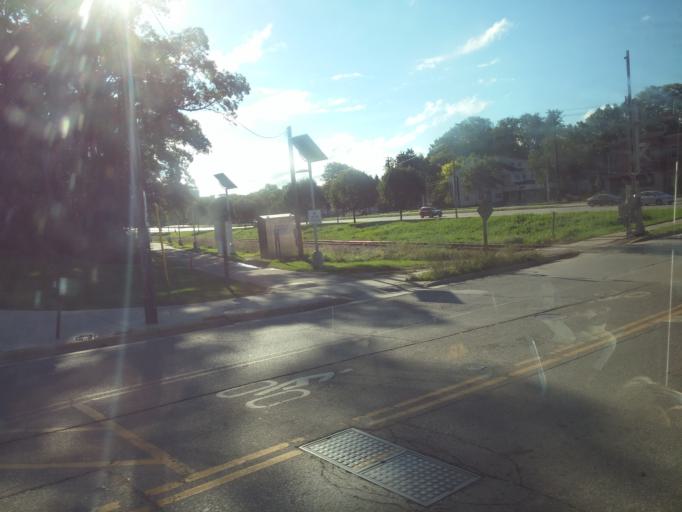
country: US
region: Wisconsin
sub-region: Dane County
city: Shorewood Hills
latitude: 43.0740
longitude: -89.4338
